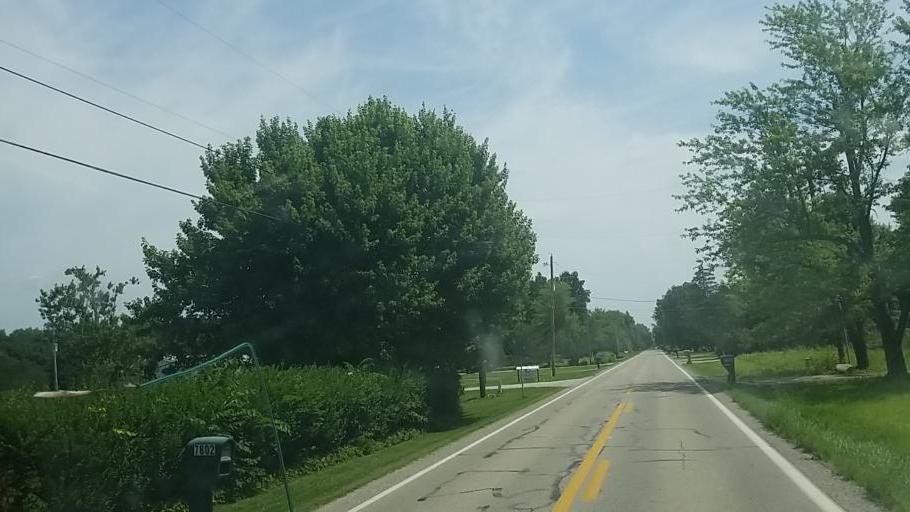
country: US
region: Ohio
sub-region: Franklin County
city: New Albany
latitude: 40.0518
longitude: -82.7829
